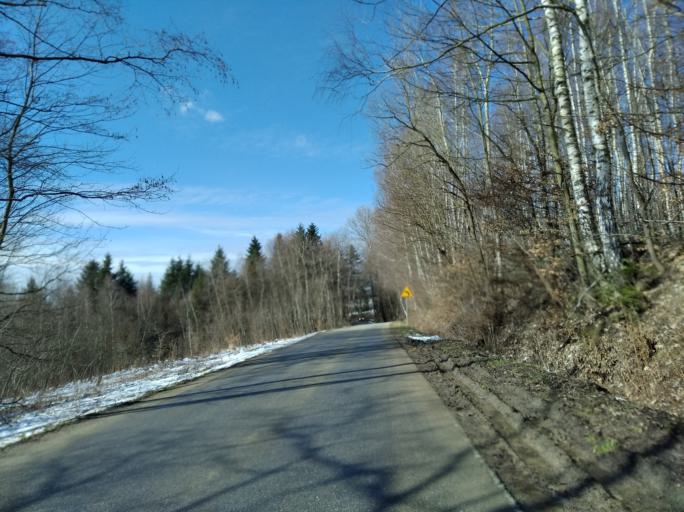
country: PL
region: Subcarpathian Voivodeship
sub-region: Powiat brzozowski
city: Jablonica Polska
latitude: 49.7198
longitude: 21.8856
